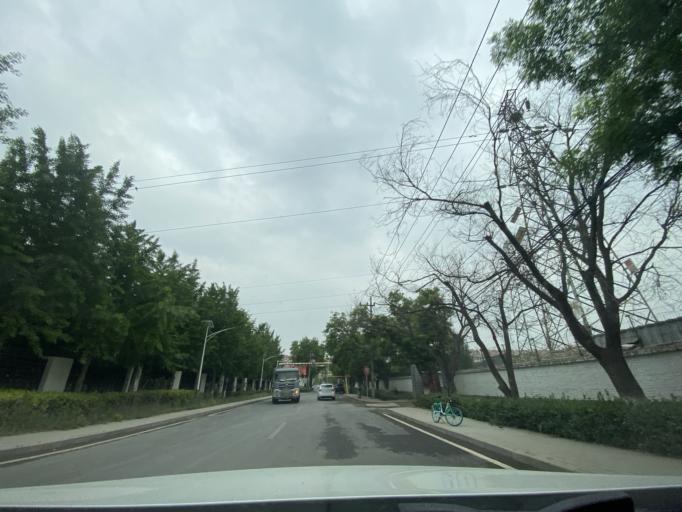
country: CN
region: Beijing
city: Sijiqing
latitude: 39.9343
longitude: 116.2389
